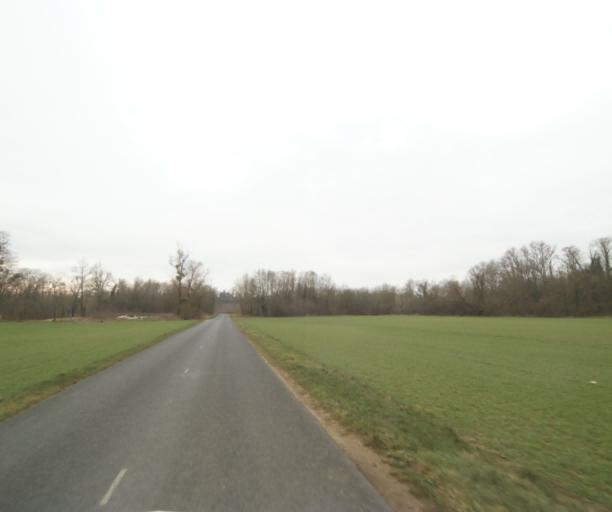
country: FR
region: Champagne-Ardenne
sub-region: Departement de la Haute-Marne
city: Villiers-en-Lieu
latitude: 48.6415
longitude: 4.8386
